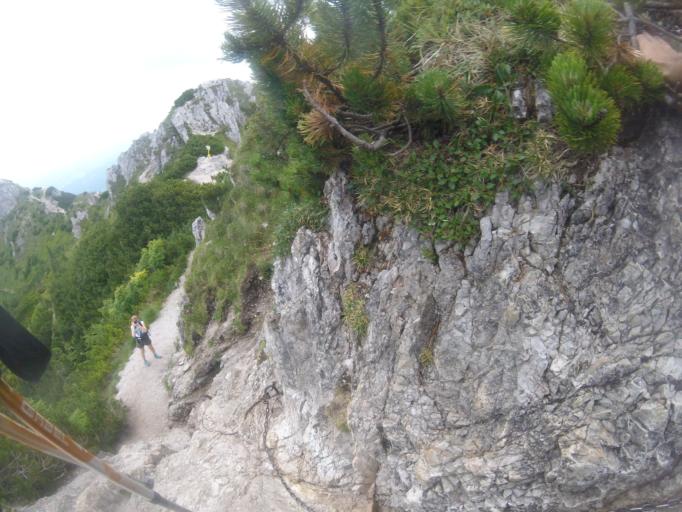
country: SK
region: Zilinsky
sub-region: Okres Zilina
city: Terchova
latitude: 49.2317
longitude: 19.0993
